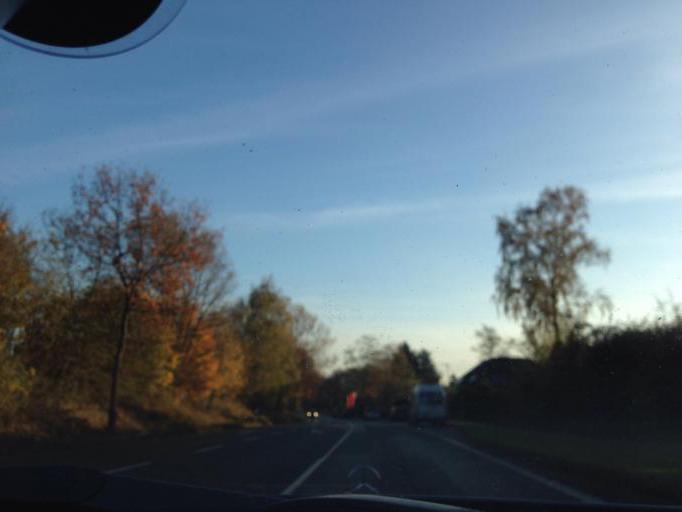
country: DE
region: Schleswig-Holstein
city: Reinbek
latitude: 53.5603
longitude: 10.2493
